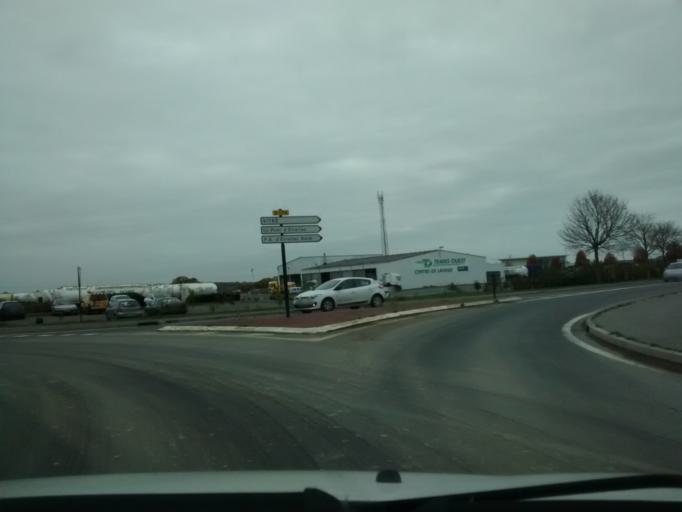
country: FR
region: Brittany
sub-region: Departement d'Ille-et-Vilaine
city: Etrelles
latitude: 48.0725
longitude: -1.1993
